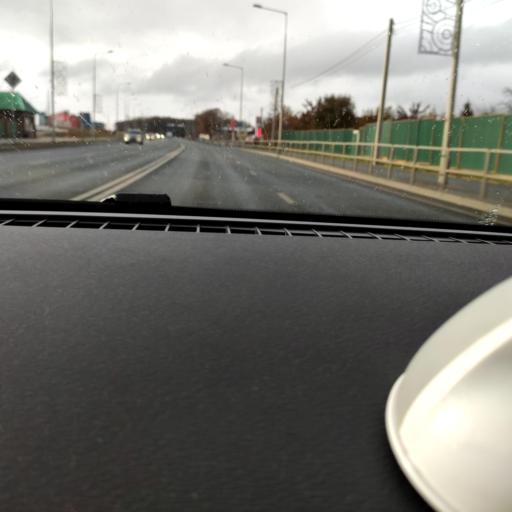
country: RU
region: Samara
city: Petra-Dubrava
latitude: 53.2767
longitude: 50.2602
